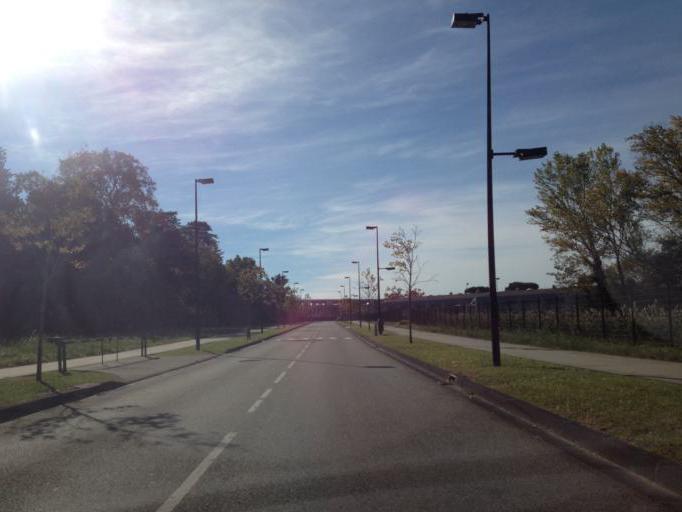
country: FR
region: Provence-Alpes-Cote d'Azur
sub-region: Departement du Vaucluse
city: Orange
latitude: 44.1309
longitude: 4.7978
